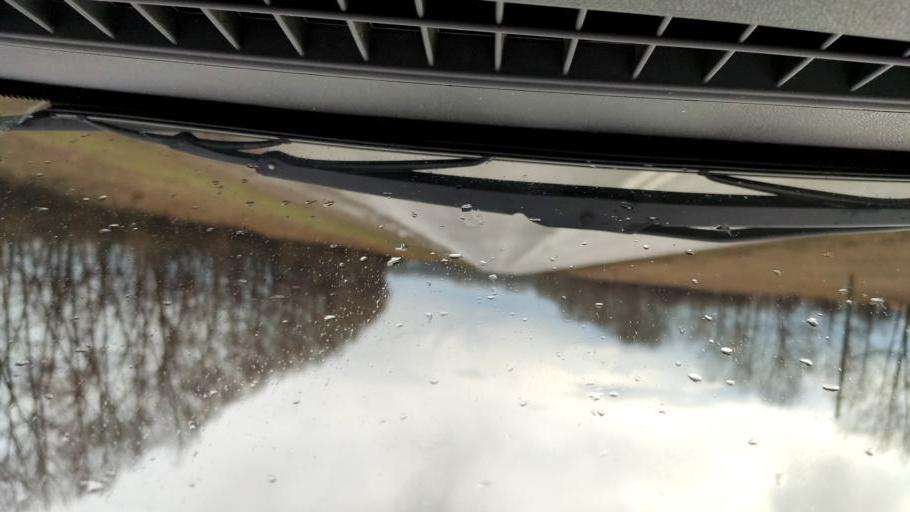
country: RU
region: Bashkortostan
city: Alekseyevka
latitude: 55.0630
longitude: 55.1006
